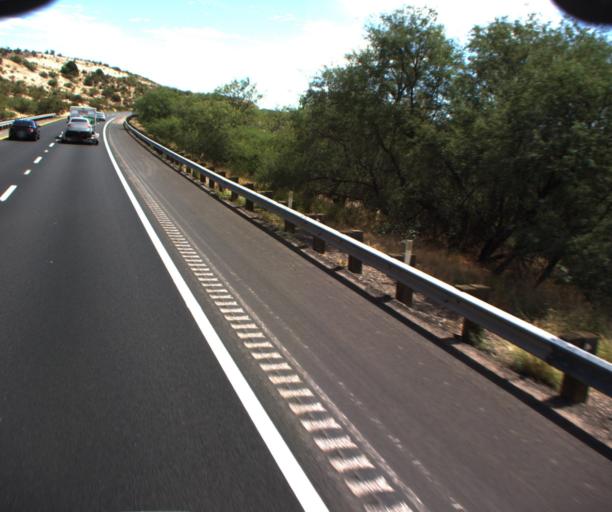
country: US
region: Arizona
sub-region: Yavapai County
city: Lake Montezuma
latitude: 34.6331
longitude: -111.8311
